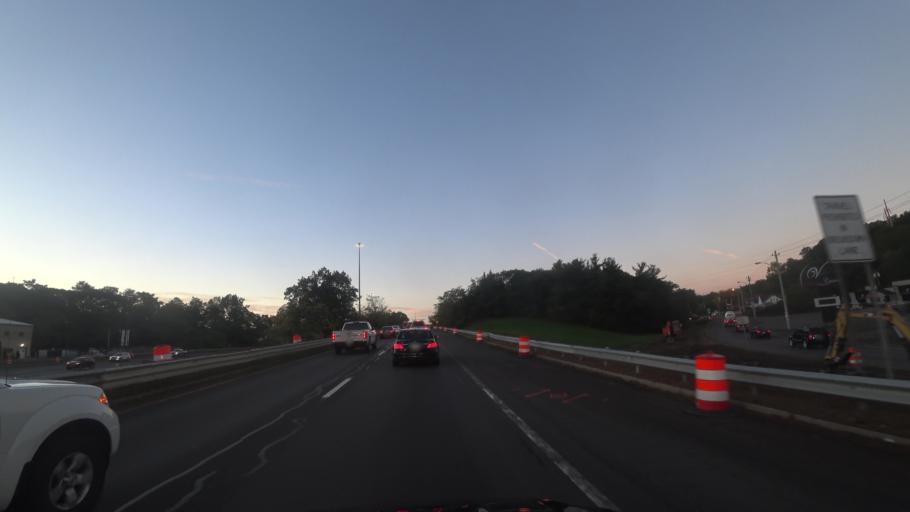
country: US
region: Massachusetts
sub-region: Essex County
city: Saugus
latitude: 42.4530
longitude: -71.0236
